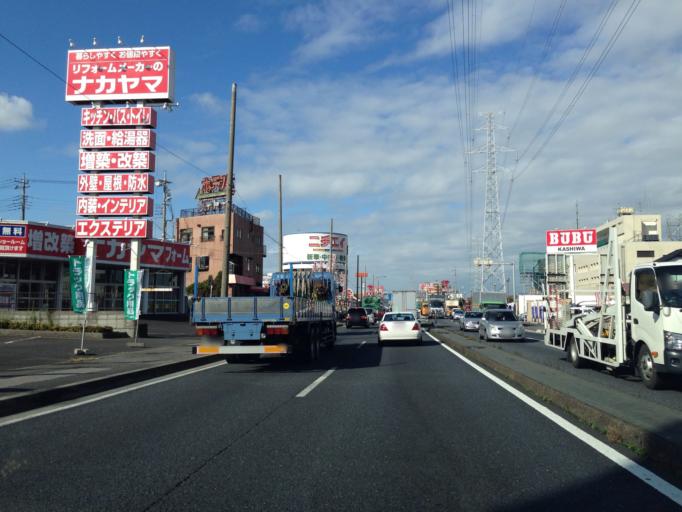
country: JP
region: Chiba
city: Kashiwa
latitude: 35.8861
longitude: 139.9630
